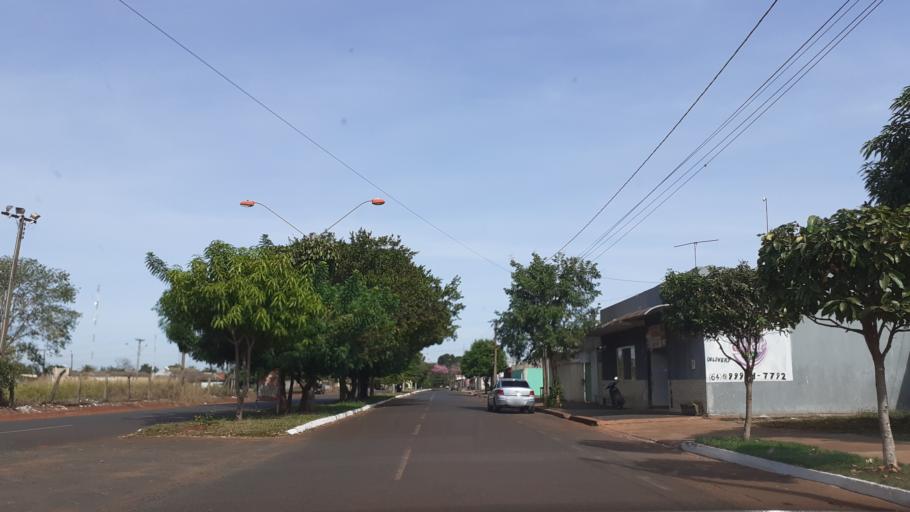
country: BR
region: Goias
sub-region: Itumbiara
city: Itumbiara
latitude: -18.4106
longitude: -49.2565
